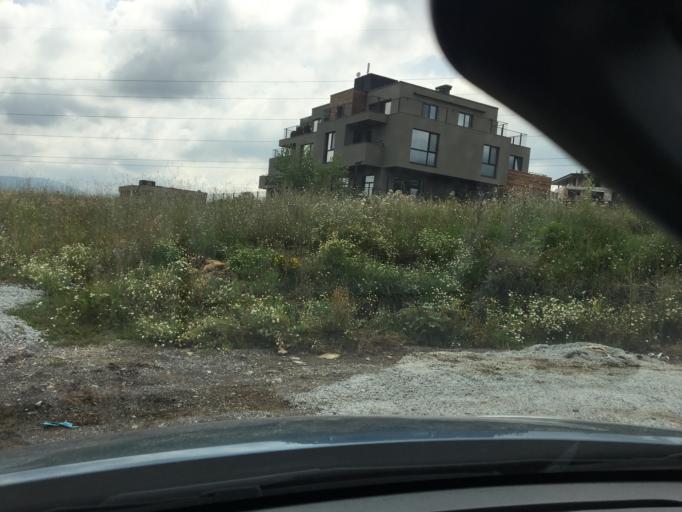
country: BG
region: Sofia-Capital
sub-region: Stolichna Obshtina
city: Sofia
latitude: 42.6161
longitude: 23.3613
